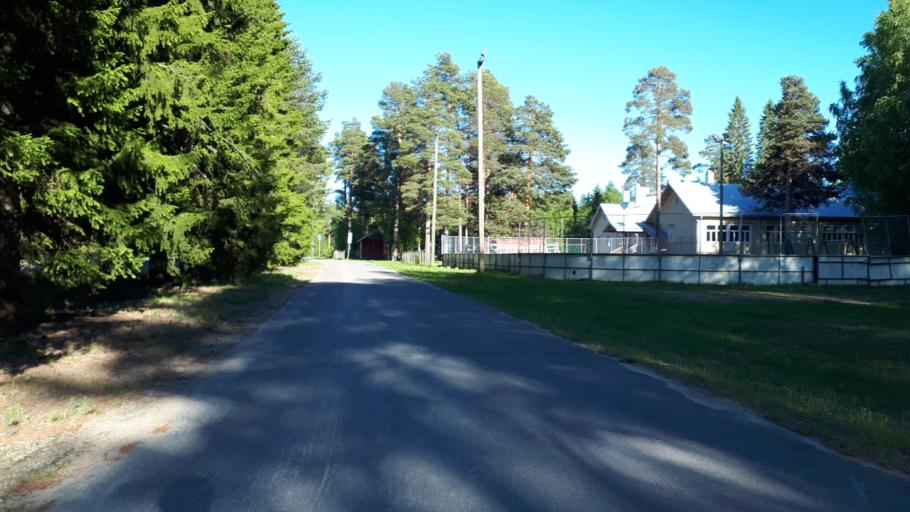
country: FI
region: Northern Ostrobothnia
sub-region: Oulunkaari
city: Ii
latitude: 65.3243
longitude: 25.4828
